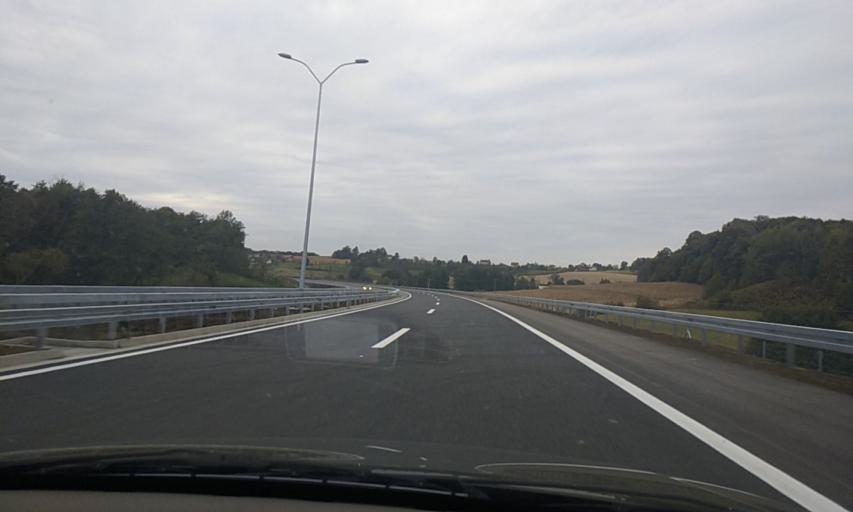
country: BA
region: Republika Srpska
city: Prnjavor
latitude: 44.8696
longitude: 17.5029
